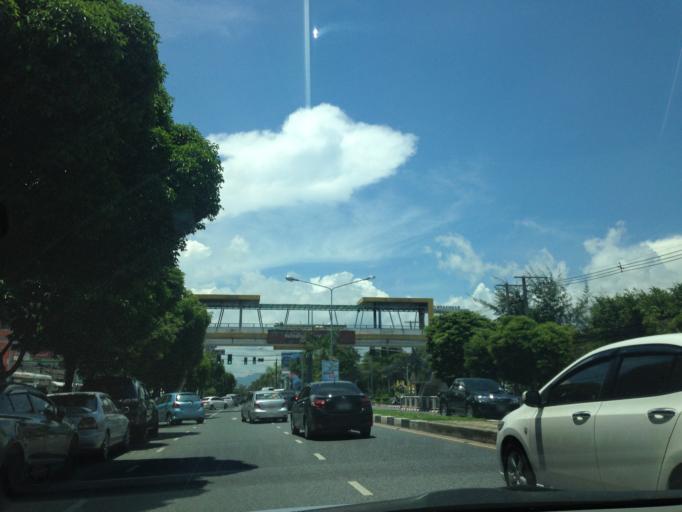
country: TH
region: Chon Buri
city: Chon Buri
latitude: 13.2860
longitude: 100.9243
